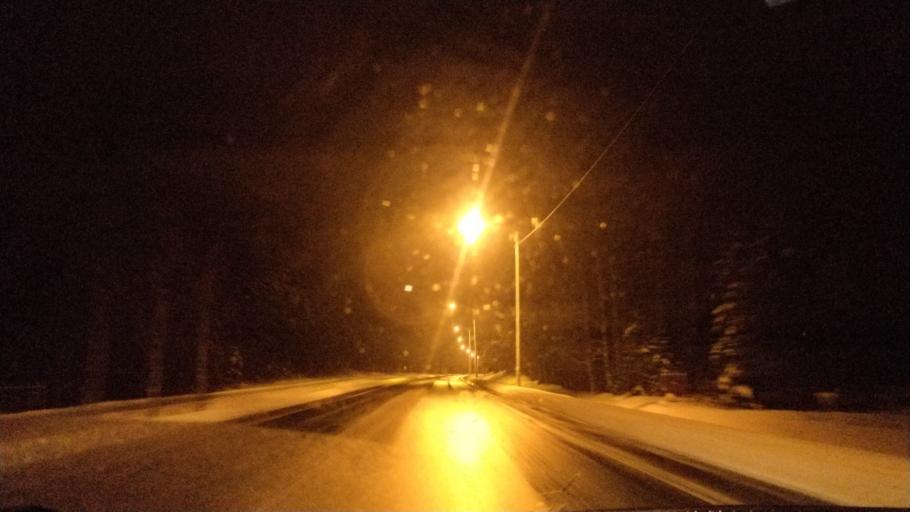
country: FI
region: Lapland
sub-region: Kemi-Tornio
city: Tervola
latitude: 66.1367
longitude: 24.9307
